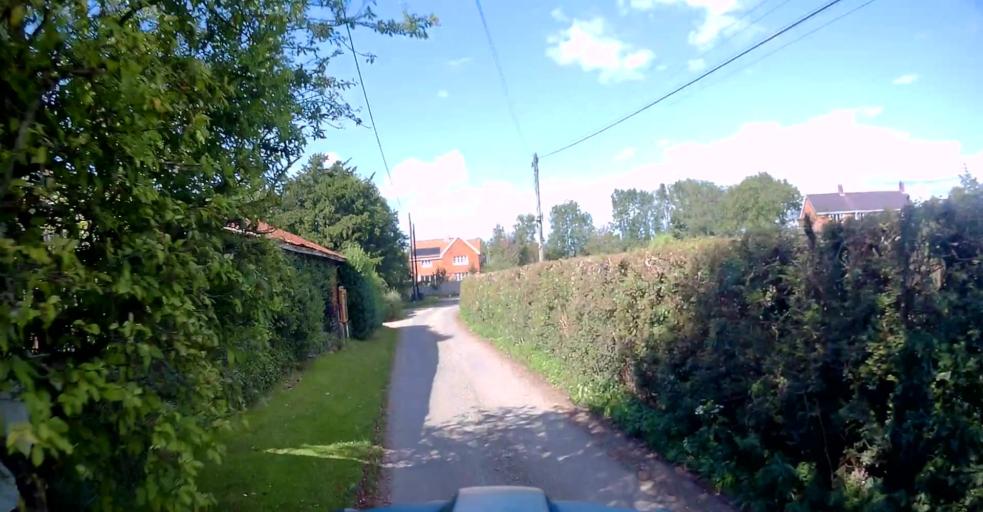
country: GB
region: England
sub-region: Hampshire
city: Four Marks
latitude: 51.1585
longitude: -1.0914
